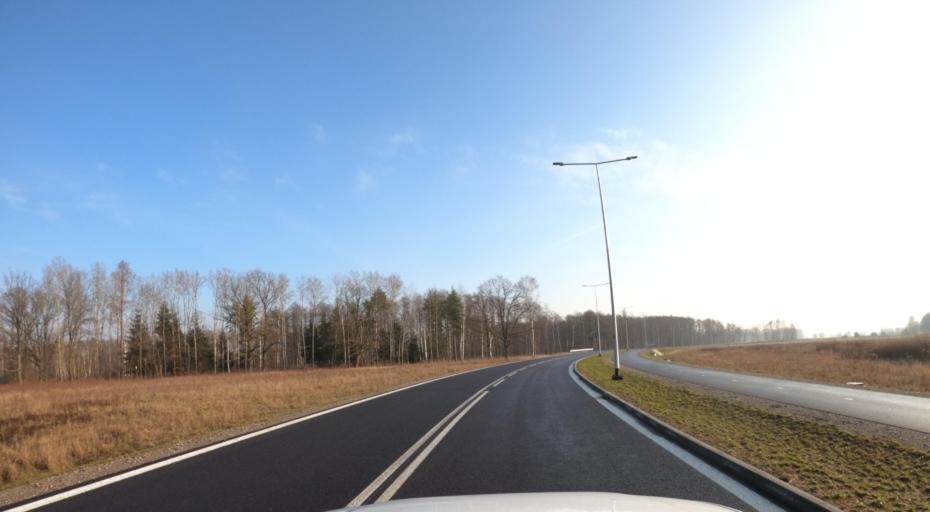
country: PL
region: Lubusz
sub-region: Powiat gorzowski
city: Kostrzyn nad Odra
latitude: 52.6292
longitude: 14.6163
